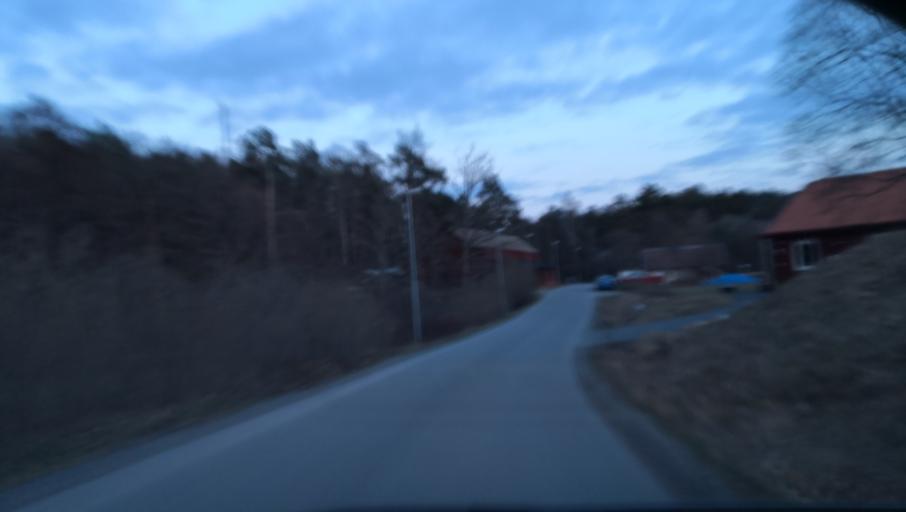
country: SE
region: Stockholm
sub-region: Nacka Kommun
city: Boo
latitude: 59.3315
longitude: 18.3152
